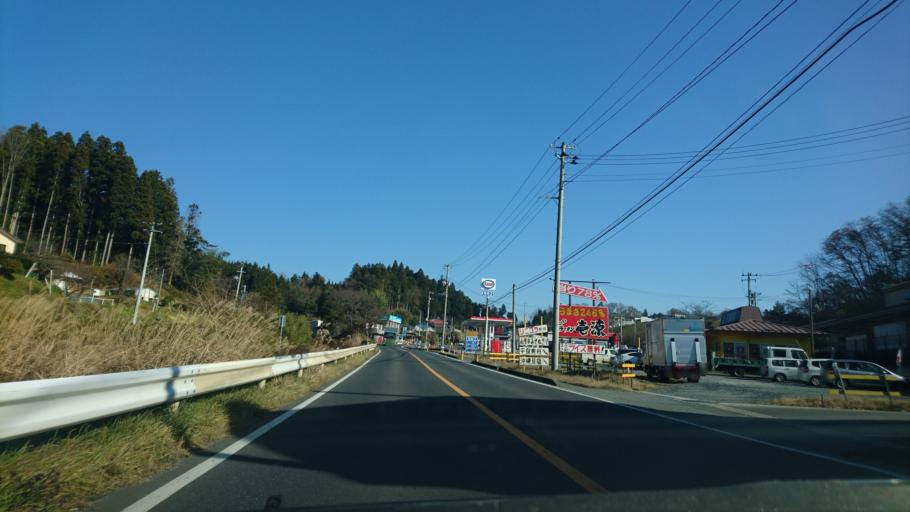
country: JP
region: Iwate
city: Ichinoseki
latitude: 38.9259
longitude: 141.3556
